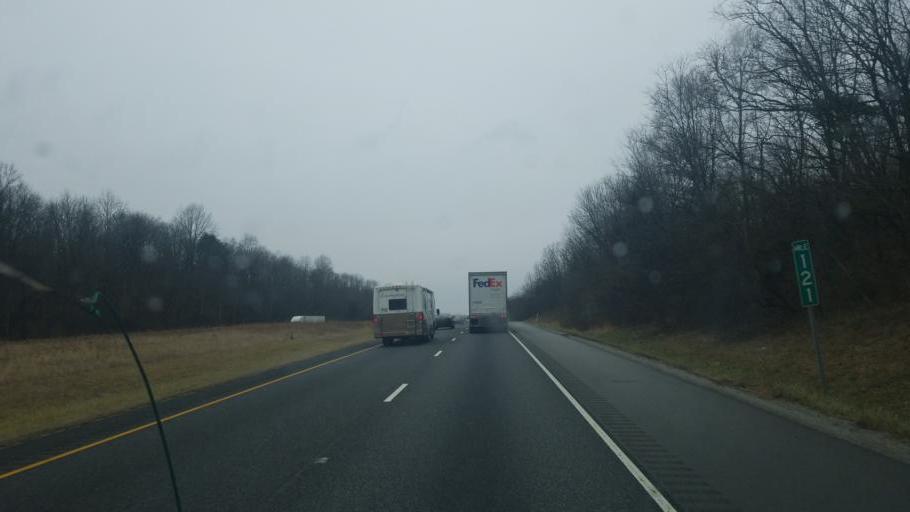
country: US
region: Indiana
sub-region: Henry County
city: Knightstown
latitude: 39.8541
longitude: -85.4512
